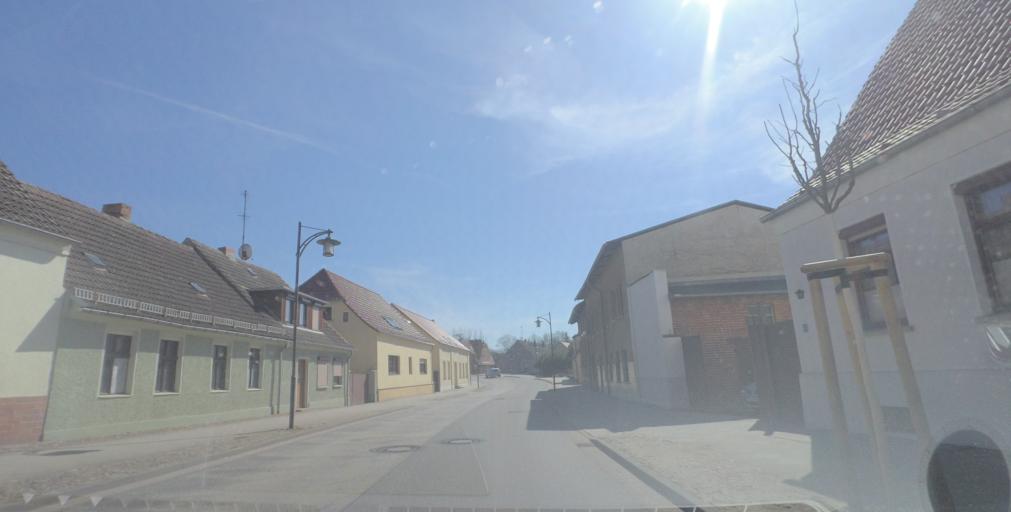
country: DE
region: Brandenburg
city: Neuruppin
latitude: 52.9486
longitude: 12.8439
